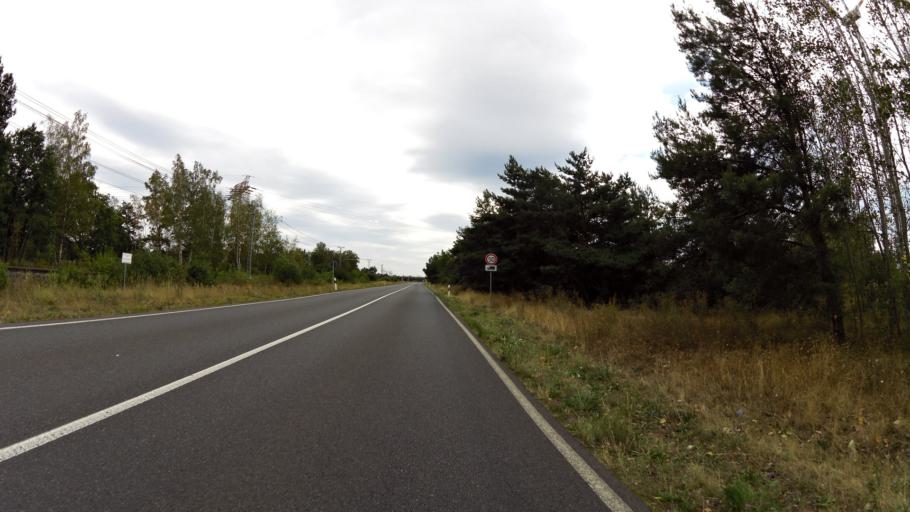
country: DE
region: Brandenburg
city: Heinersbruck
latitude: 51.7960
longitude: 14.4839
